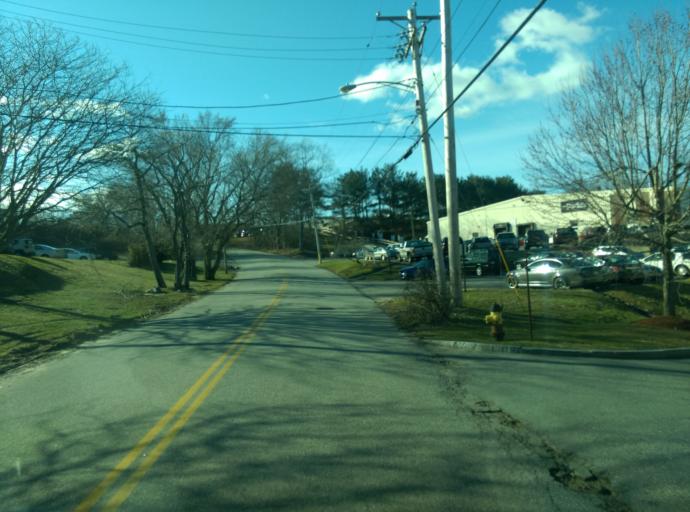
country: US
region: Massachusetts
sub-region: Essex County
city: Haverhill
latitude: 42.7570
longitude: -71.1224
